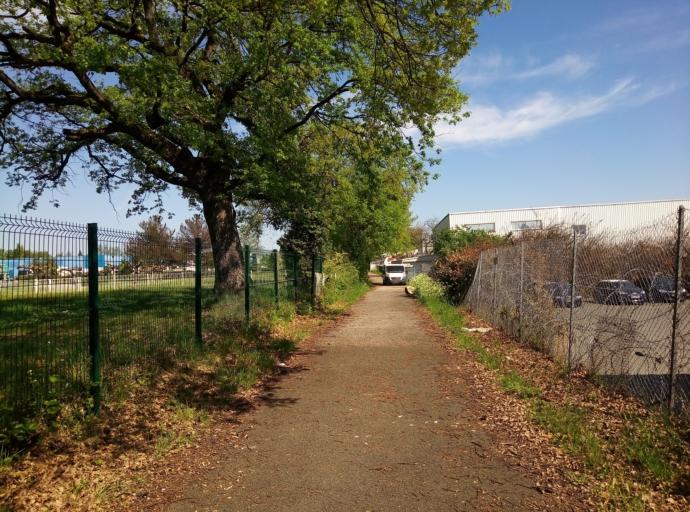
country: FR
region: Aquitaine
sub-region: Departement de la Gironde
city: Lormont
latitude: 44.8787
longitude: -0.5151
